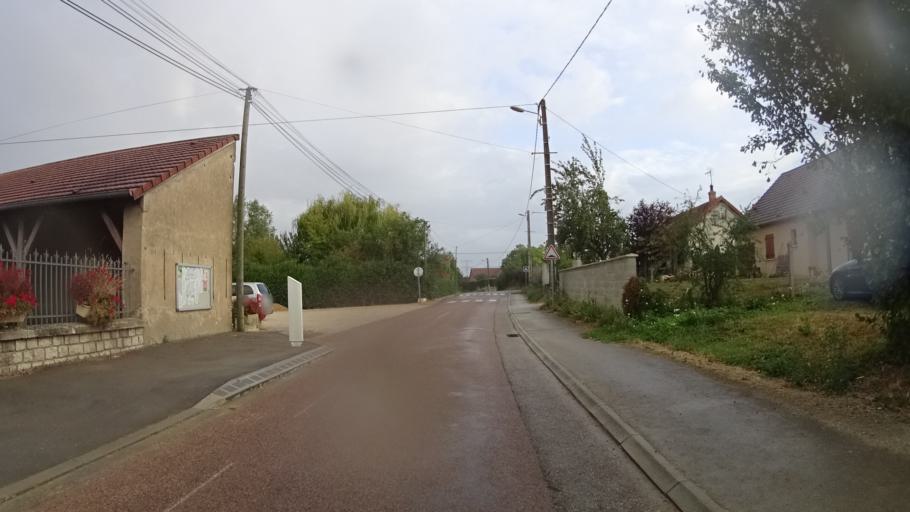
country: FR
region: Bourgogne
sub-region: Departement de Saone-et-Loire
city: Verdun-sur-le-Doubs
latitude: 46.9606
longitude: 5.0264
